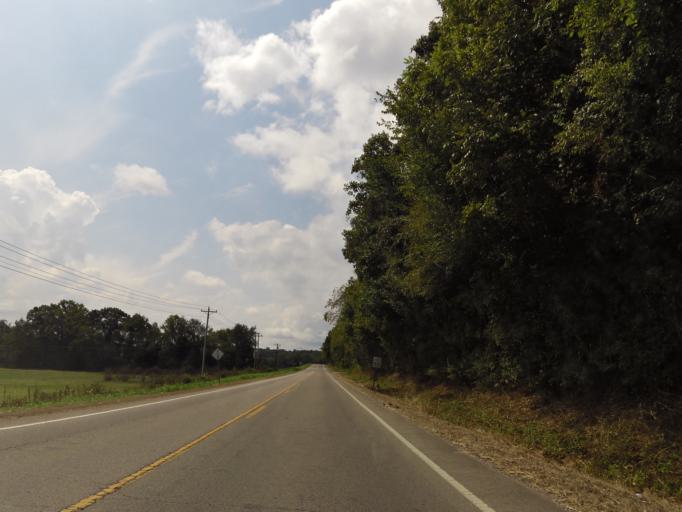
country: US
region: Tennessee
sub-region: Perry County
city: Linden
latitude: 35.7592
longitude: -87.7838
